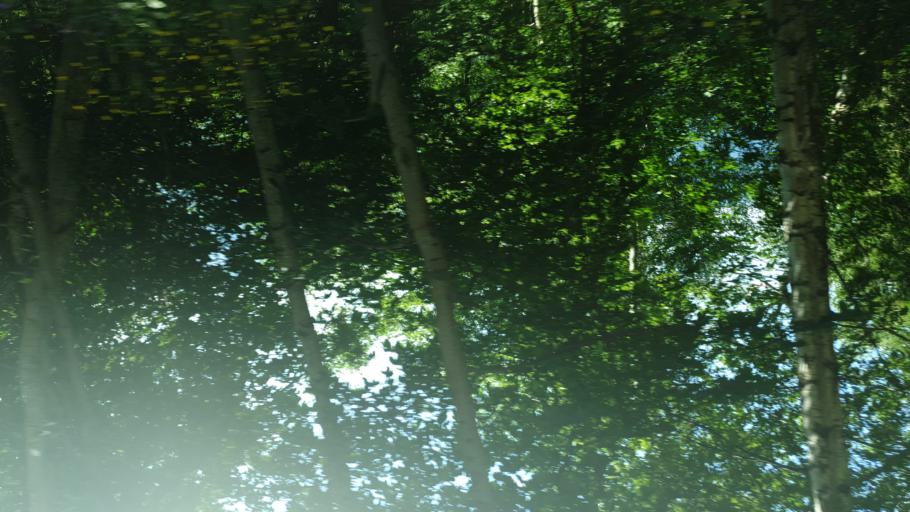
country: NO
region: Nord-Trondelag
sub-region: Leksvik
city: Leksvik
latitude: 63.6974
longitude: 10.7218
